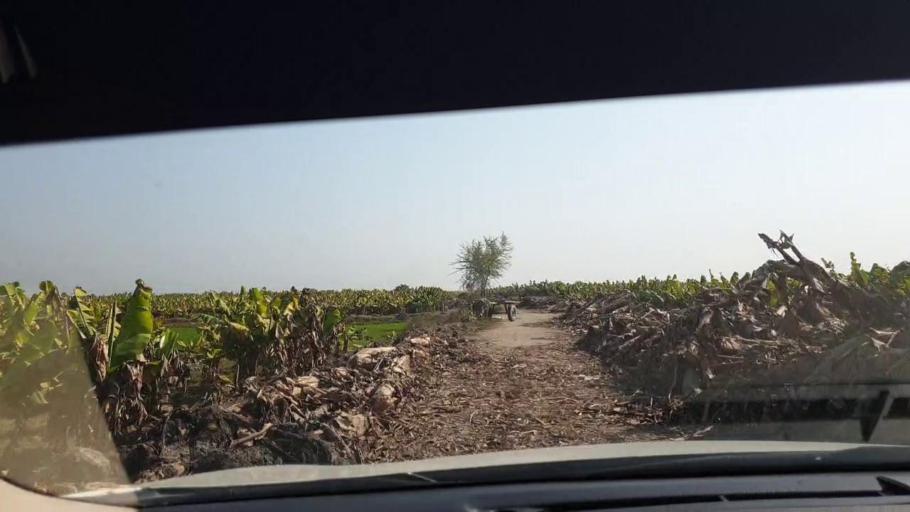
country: PK
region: Sindh
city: Tando Adam
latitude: 25.7403
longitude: 68.7039
